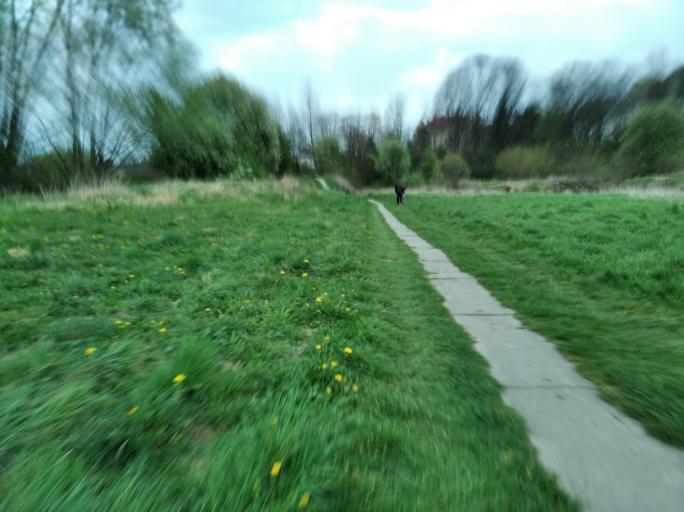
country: PL
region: Subcarpathian Voivodeship
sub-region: Powiat strzyzowski
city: Strzyzow
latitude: 49.8654
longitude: 21.7984
